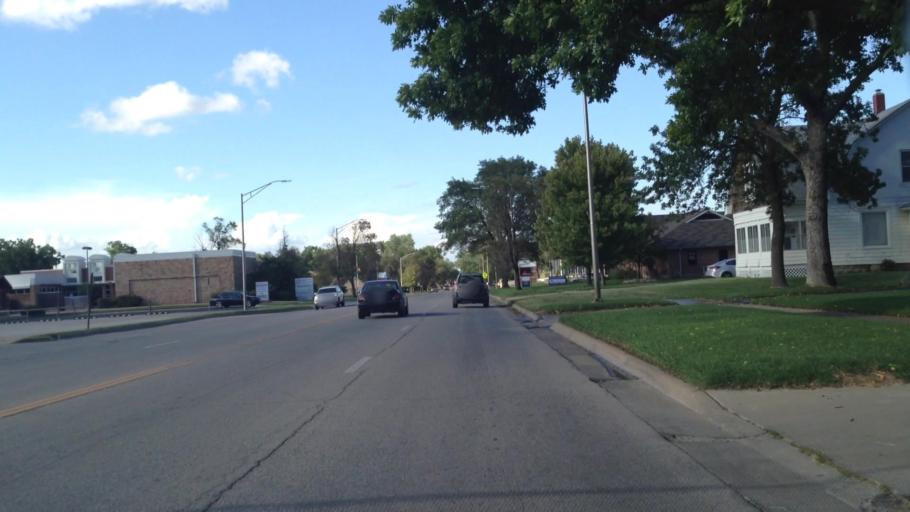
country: US
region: Kansas
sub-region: Franklin County
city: Ottawa
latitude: 38.5948
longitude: -95.2687
